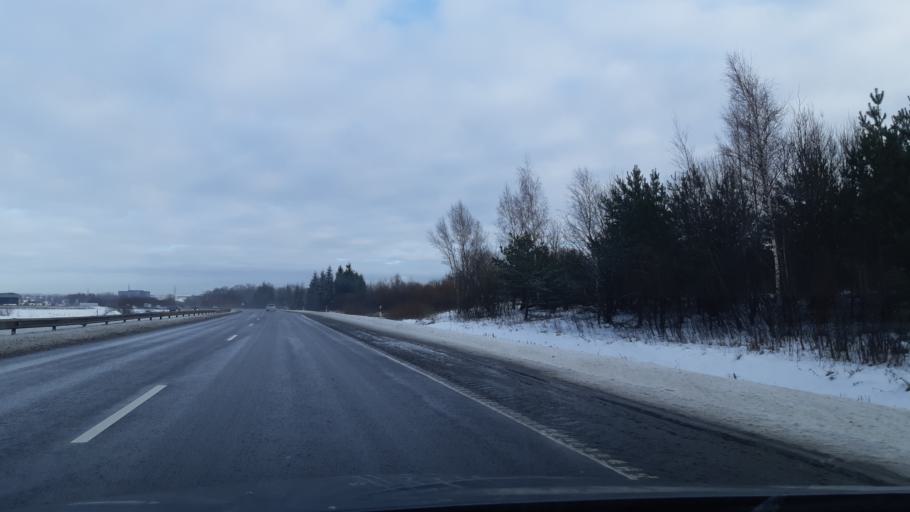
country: LT
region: Kauno apskritis
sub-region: Kaunas
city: Silainiai
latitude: 54.9289
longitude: 23.8581
